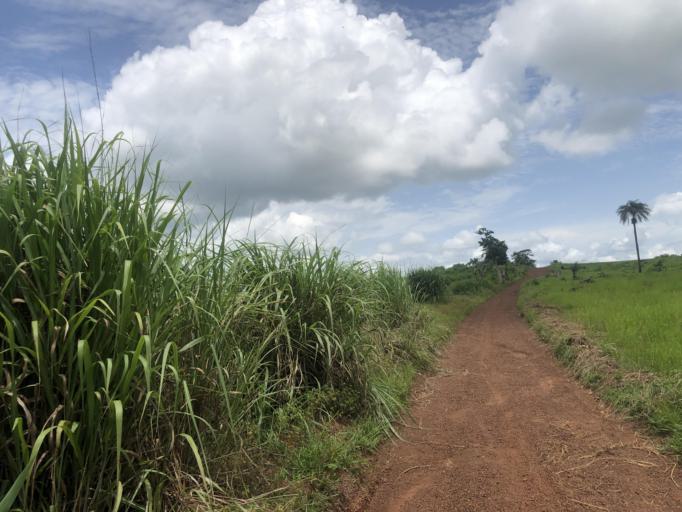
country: SL
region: Northern Province
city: Magburaka
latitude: 8.6914
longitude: -11.9437
